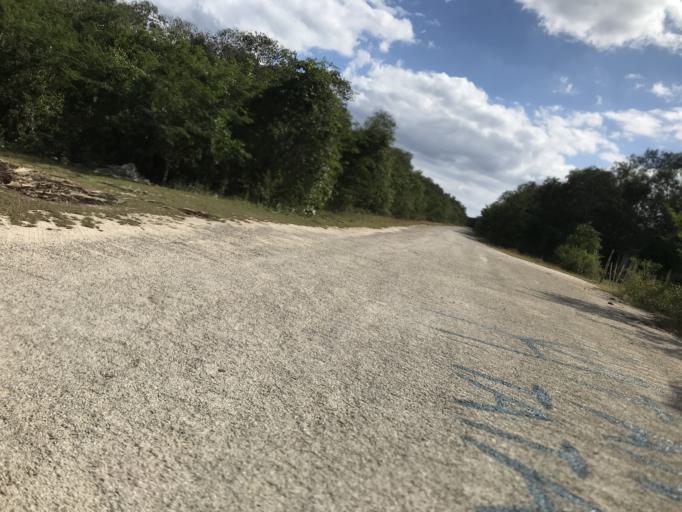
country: CU
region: Cienfuegos
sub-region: Municipio de Aguada de Pasajeros
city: Aguada de Pasajeros
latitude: 22.0754
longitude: -81.0367
